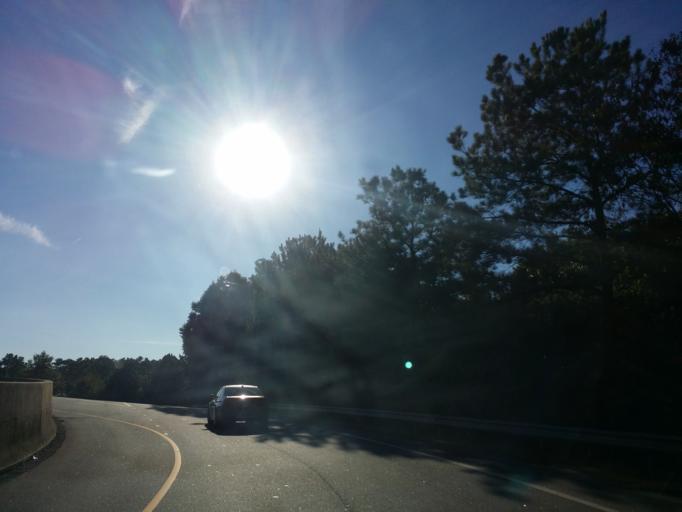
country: US
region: North Carolina
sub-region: Wake County
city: Raleigh
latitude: 35.7706
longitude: -78.6455
